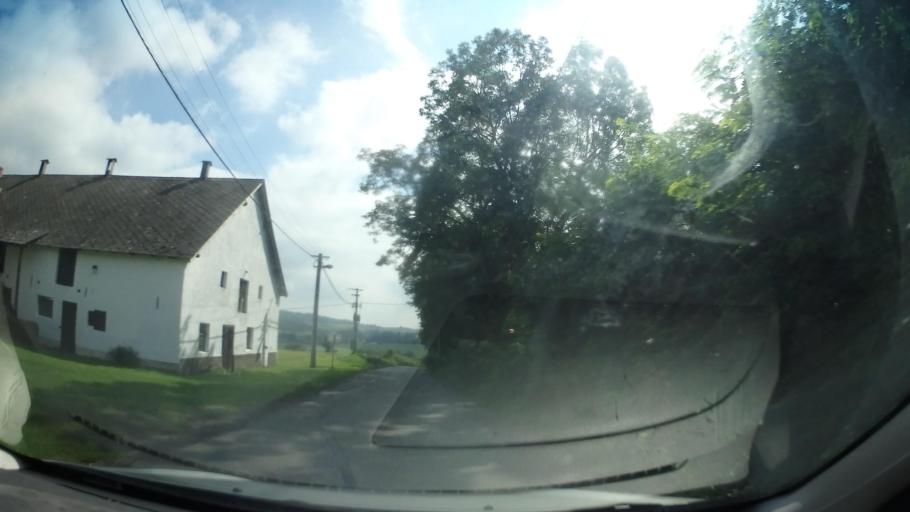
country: CZ
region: Central Bohemia
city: Sedlcany
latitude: 49.7099
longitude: 14.3728
